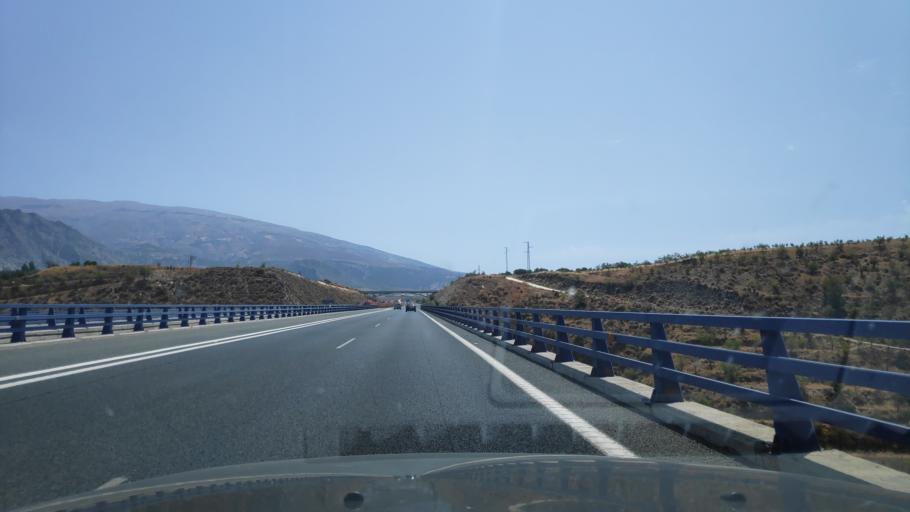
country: ES
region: Andalusia
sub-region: Provincia de Granada
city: Durcal
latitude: 36.9846
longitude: -3.5852
